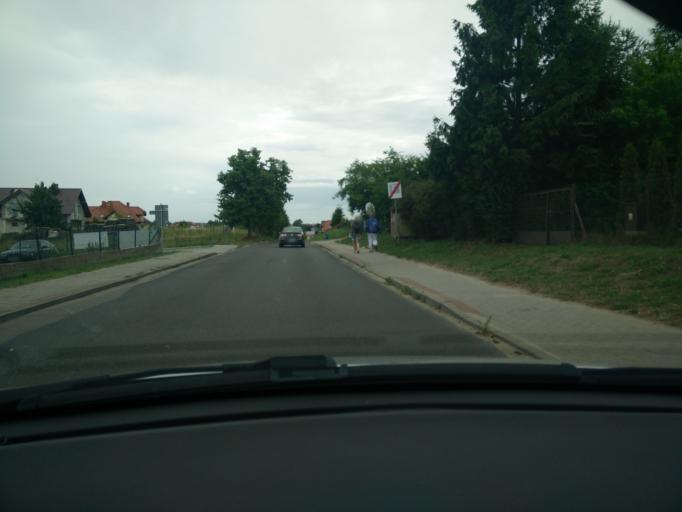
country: PL
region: Pomeranian Voivodeship
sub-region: Powiat pucki
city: Mosty
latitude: 54.6290
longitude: 18.4968
